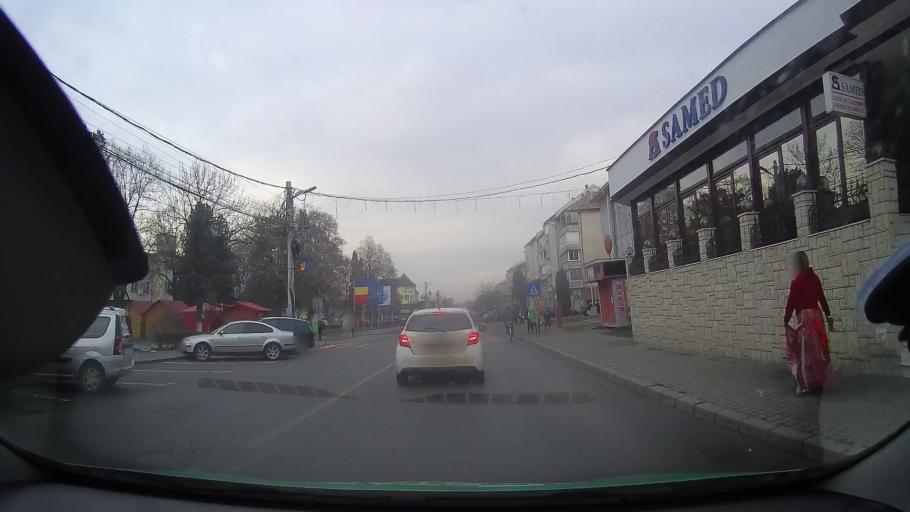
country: RO
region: Mures
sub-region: Comuna Ludus
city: Ludus
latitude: 46.4742
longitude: 24.0954
